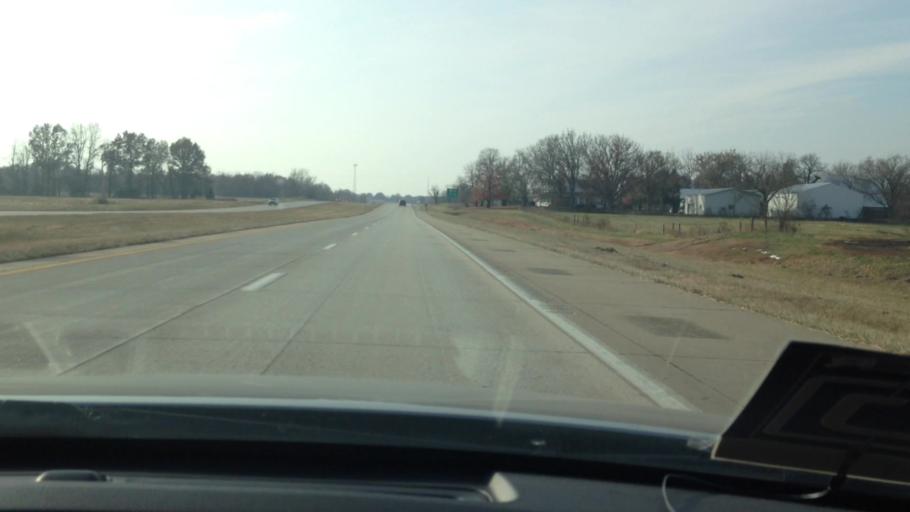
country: US
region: Missouri
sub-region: Henry County
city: Clinton
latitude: 38.4640
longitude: -93.9777
